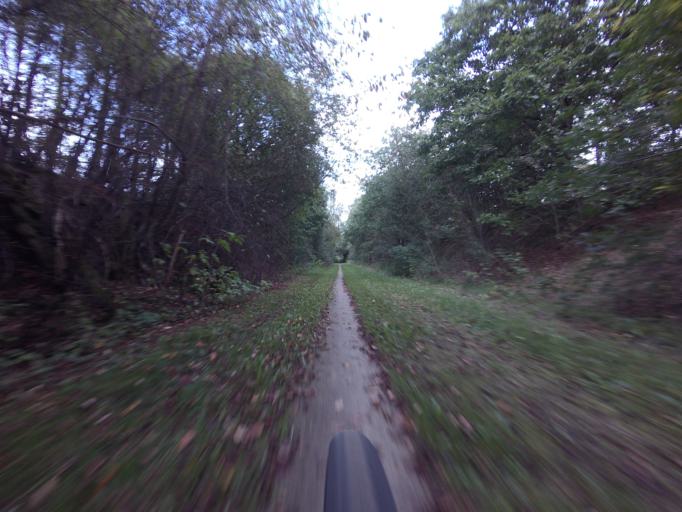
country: DK
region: Central Jutland
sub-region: Ikast-Brande Kommune
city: Brande
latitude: 55.8808
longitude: 9.0508
